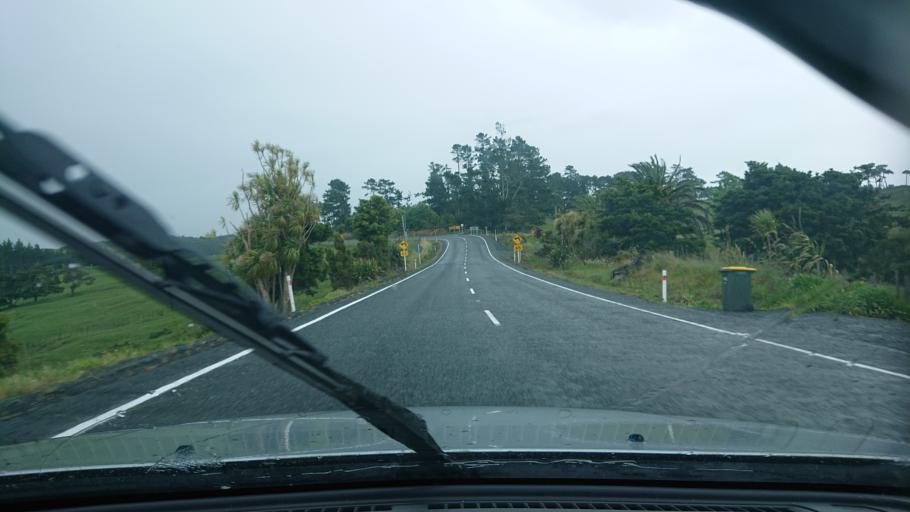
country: NZ
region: Auckland
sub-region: Auckland
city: Wellsford
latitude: -36.3353
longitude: 174.4690
